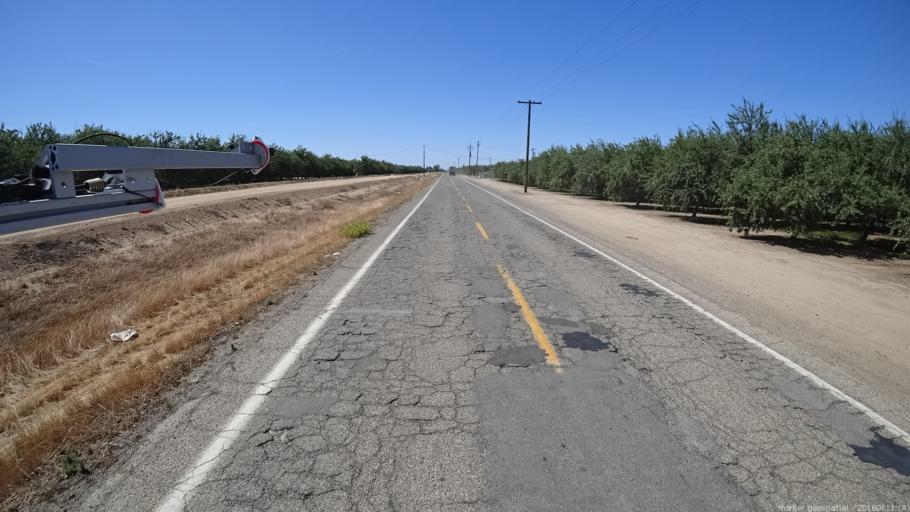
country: US
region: California
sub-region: Madera County
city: Fairmead
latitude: 37.0482
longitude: -120.2024
